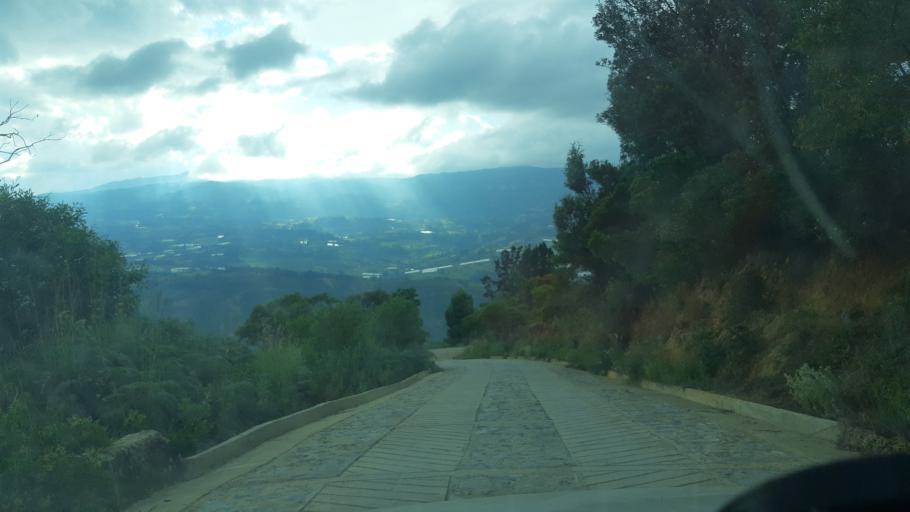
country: CO
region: Boyaca
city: Santa Sofia
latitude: 5.7447
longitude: -73.5620
